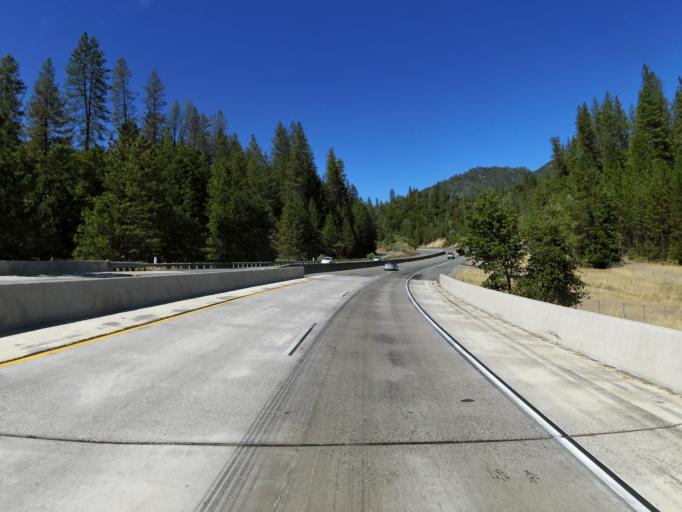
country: US
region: California
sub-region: Shasta County
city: Shasta Lake
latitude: 40.8502
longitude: -122.3416
